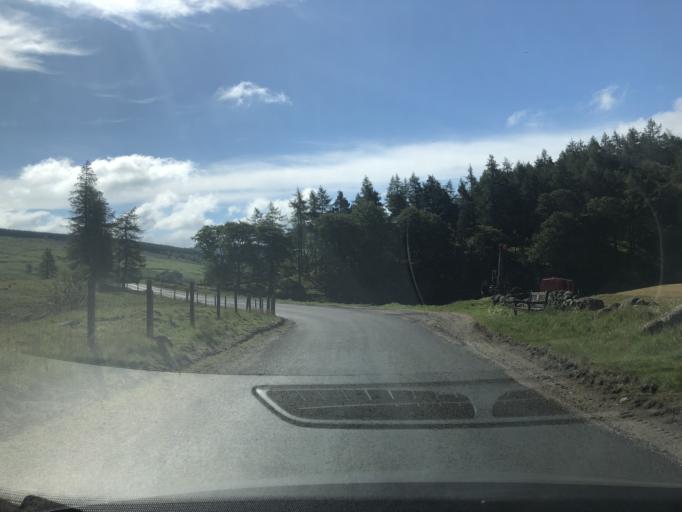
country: GB
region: Scotland
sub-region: Angus
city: Kirriemuir
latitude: 56.7676
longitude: -3.0226
